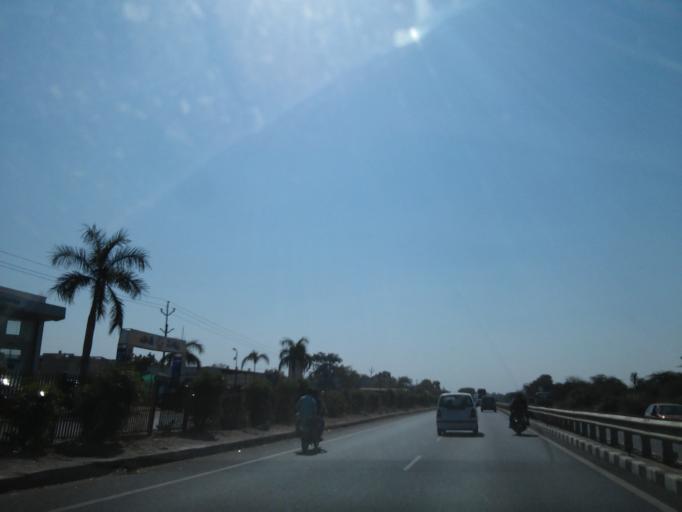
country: IN
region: Gujarat
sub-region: Sabar Kantha
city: Himatnagar
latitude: 23.5696
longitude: 72.9554
